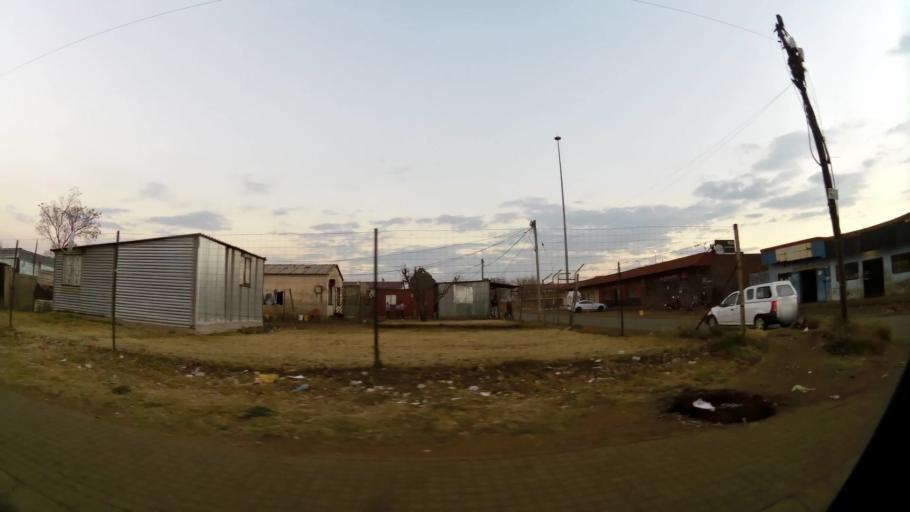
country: ZA
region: Gauteng
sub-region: City of Johannesburg Metropolitan Municipality
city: Orange Farm
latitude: -26.5543
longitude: 27.8533
